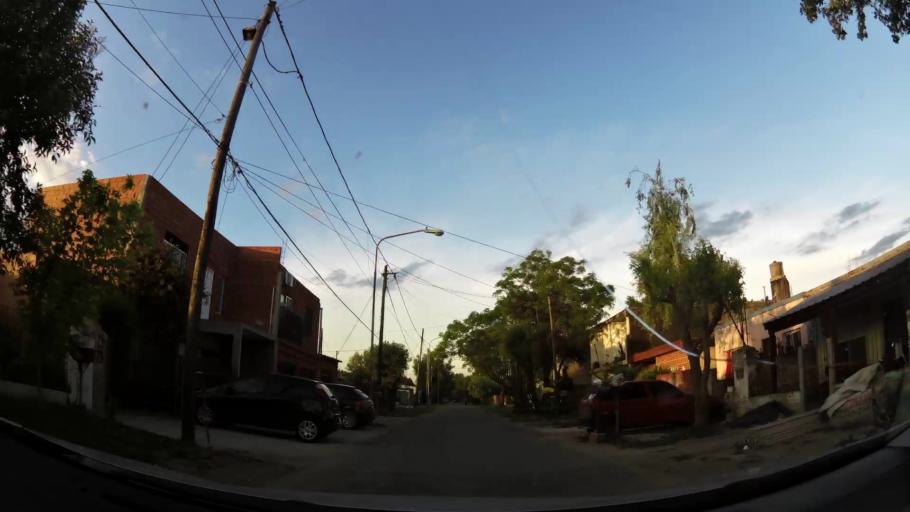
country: AR
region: Buenos Aires
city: Santa Catalina - Dique Lujan
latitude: -34.4455
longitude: -58.6613
